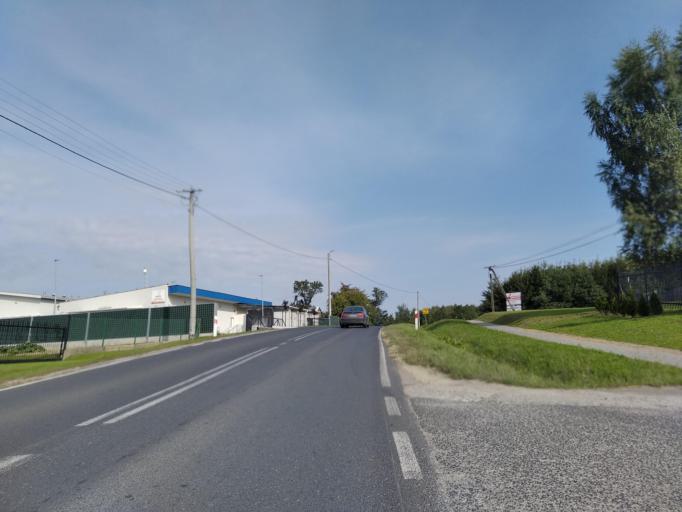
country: PL
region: Subcarpathian Voivodeship
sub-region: Powiat ropczycko-sedziszowski
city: Ostrow
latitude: 50.1009
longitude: 21.5933
